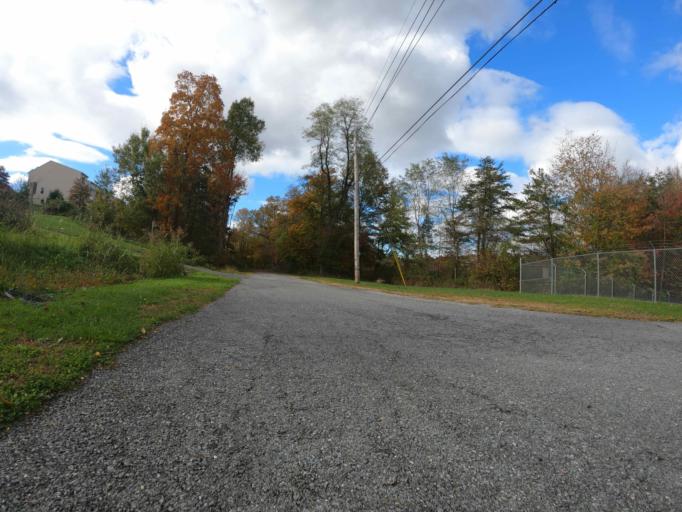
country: US
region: Maryland
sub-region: Carroll County
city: Mount Airy
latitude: 39.3673
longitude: -77.1283
